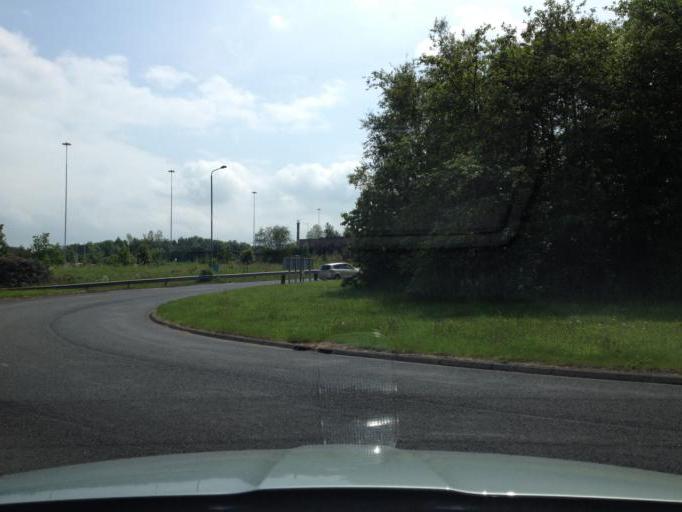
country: GB
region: Scotland
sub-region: West Dunbartonshire
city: Old Kilpatrick
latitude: 55.9134
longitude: -4.4739
